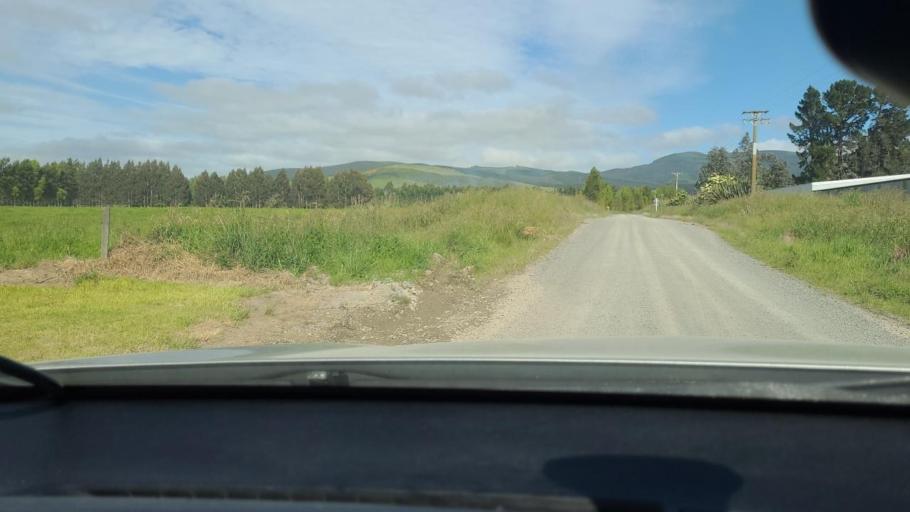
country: NZ
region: Southland
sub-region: Southland District
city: Winton
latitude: -45.9001
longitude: 168.1169
